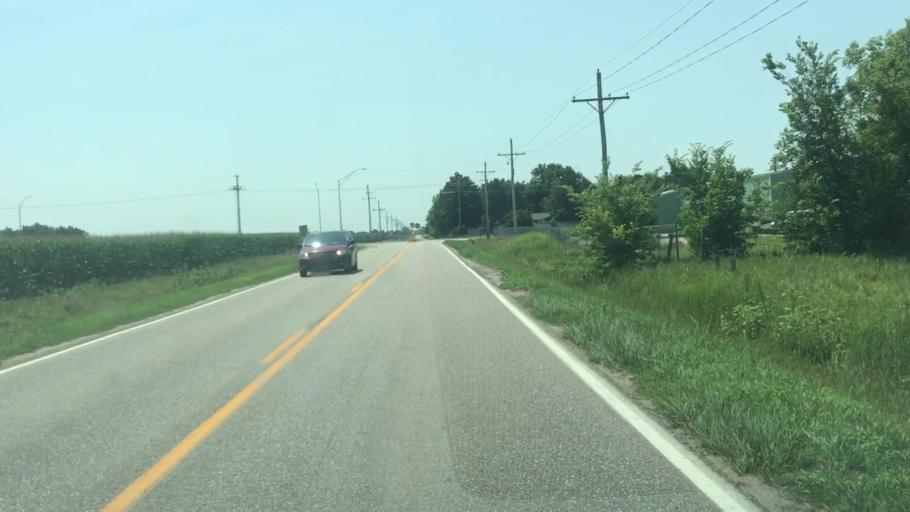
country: US
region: Nebraska
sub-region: Hall County
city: Grand Island
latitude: 40.8883
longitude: -98.3017
